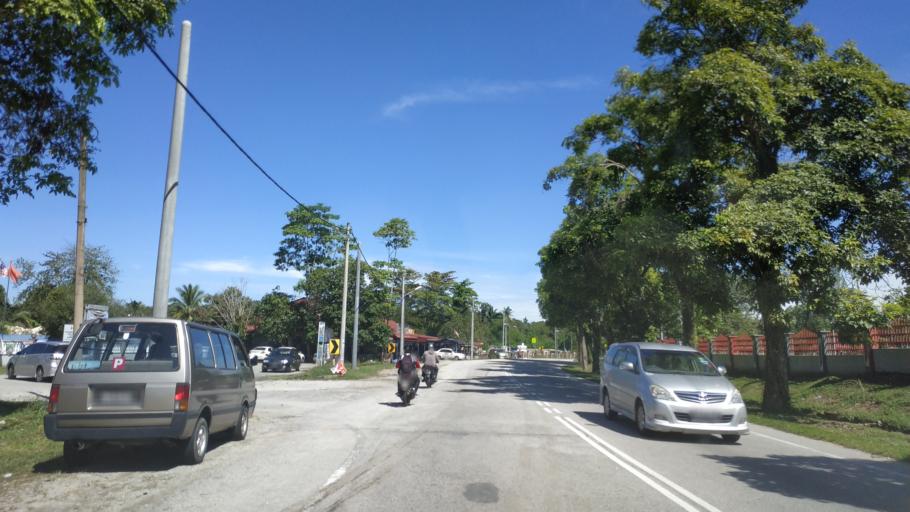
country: MY
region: Kedah
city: Kulim
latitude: 5.3503
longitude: 100.5364
